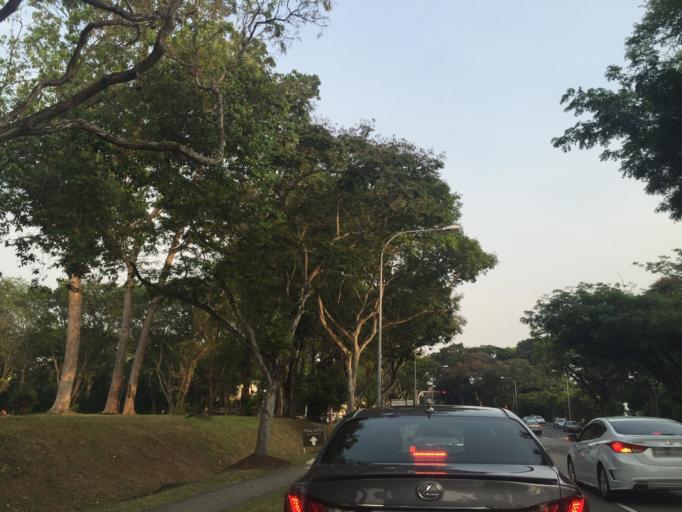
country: SG
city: Singapore
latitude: 1.3127
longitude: 103.7940
